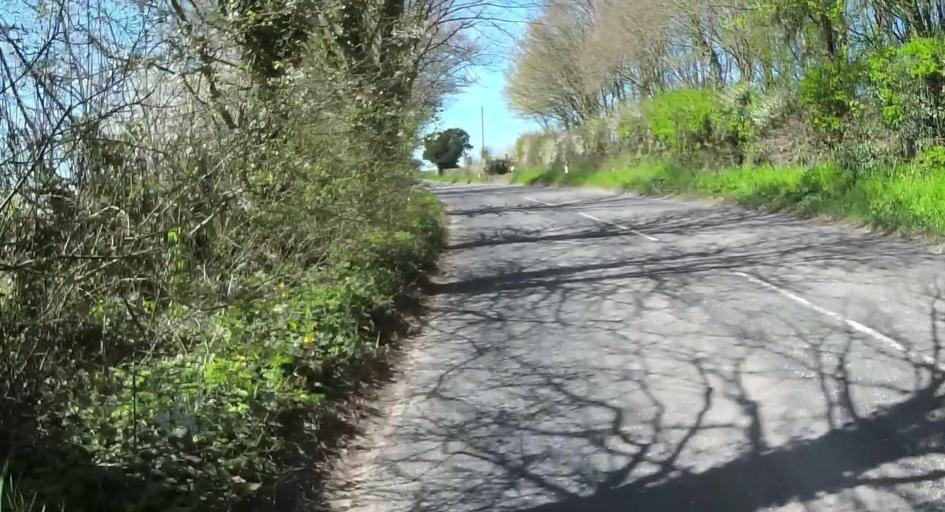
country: GB
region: England
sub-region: Hampshire
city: Winchester
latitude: 51.1008
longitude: -1.3653
